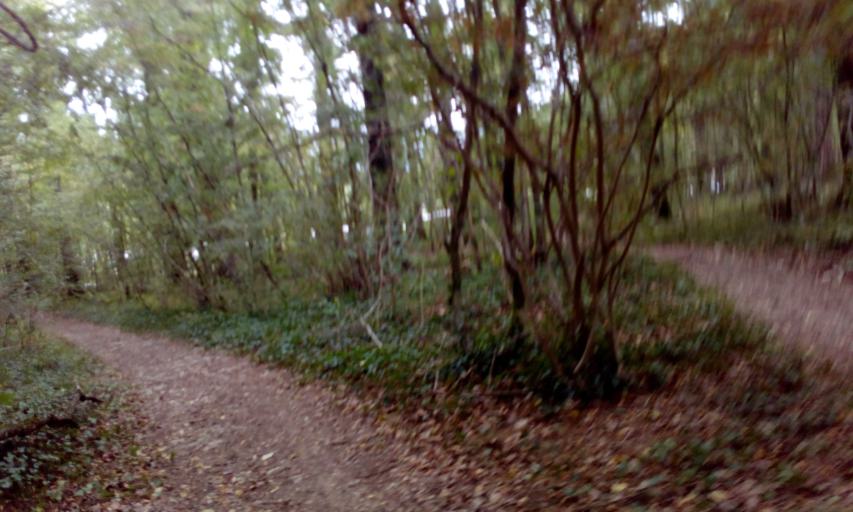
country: BE
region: Wallonia
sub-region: Province du Luxembourg
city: Wellin
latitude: 50.1139
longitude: 5.1309
